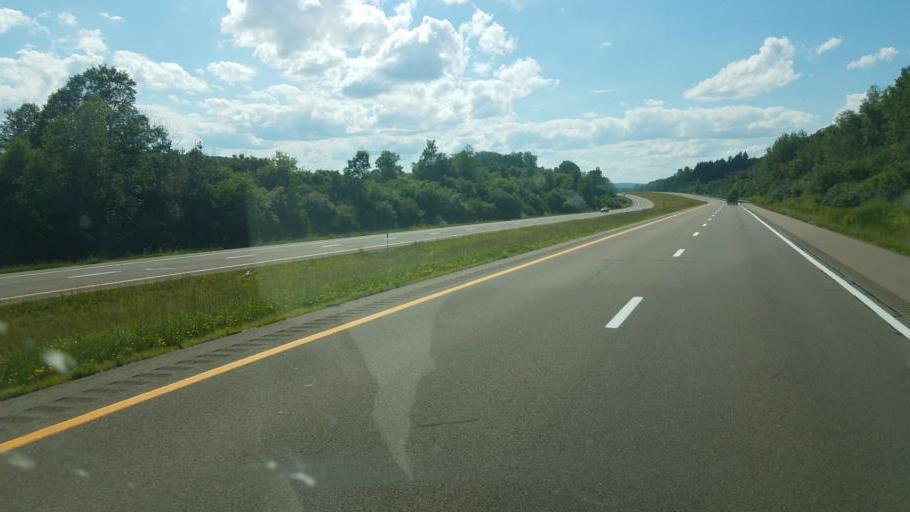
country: US
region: New York
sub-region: Steuben County
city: Hornell
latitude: 42.3723
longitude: -77.6286
